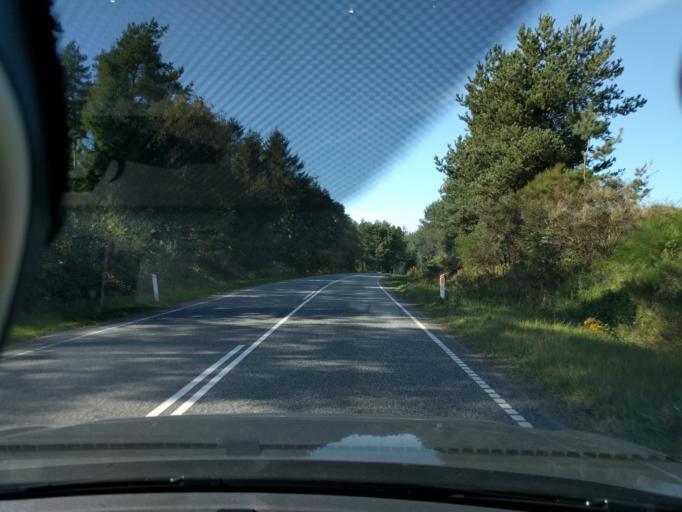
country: DK
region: North Denmark
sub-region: Mariagerfjord Kommune
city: Hobro
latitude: 56.6703
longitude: 9.7054
